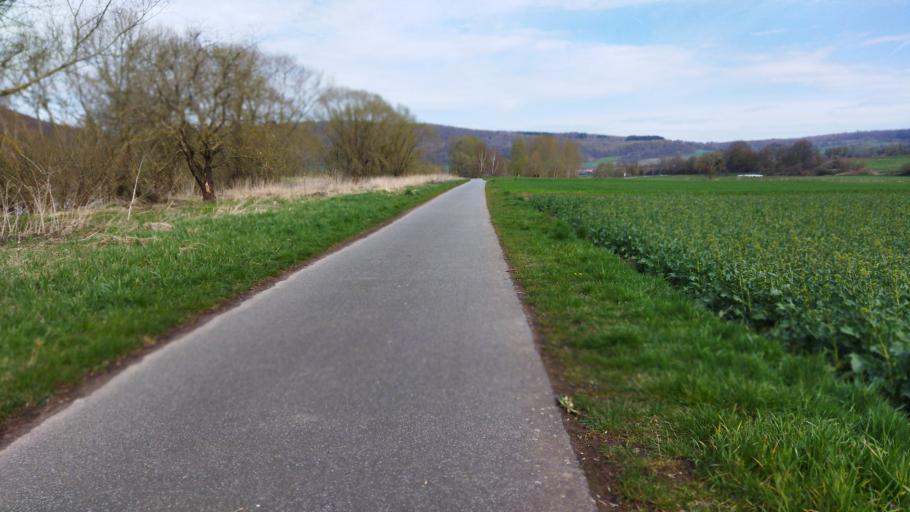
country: DE
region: Lower Saxony
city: Bodenfelde
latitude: 51.5730
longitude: 9.5926
